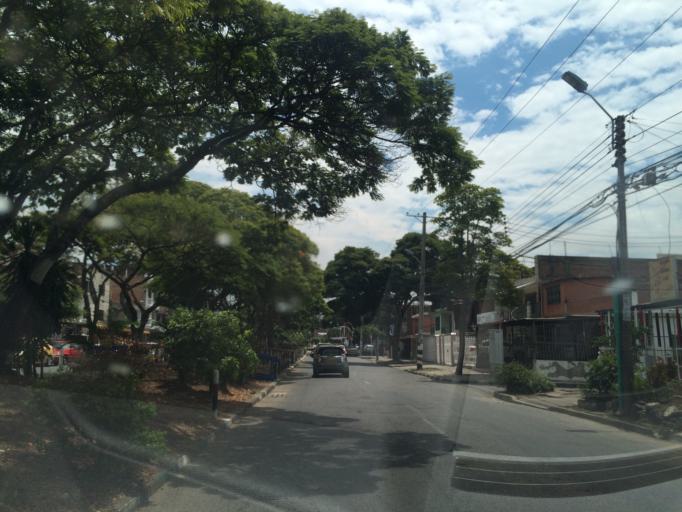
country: CO
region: Valle del Cauca
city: Cali
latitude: 3.4173
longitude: -76.5246
